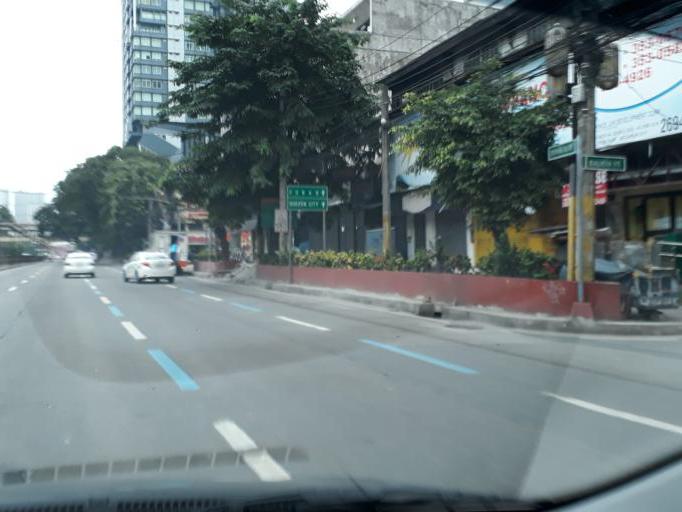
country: PH
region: Metro Manila
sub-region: City of Manila
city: Manila
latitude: 14.6069
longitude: 120.9900
